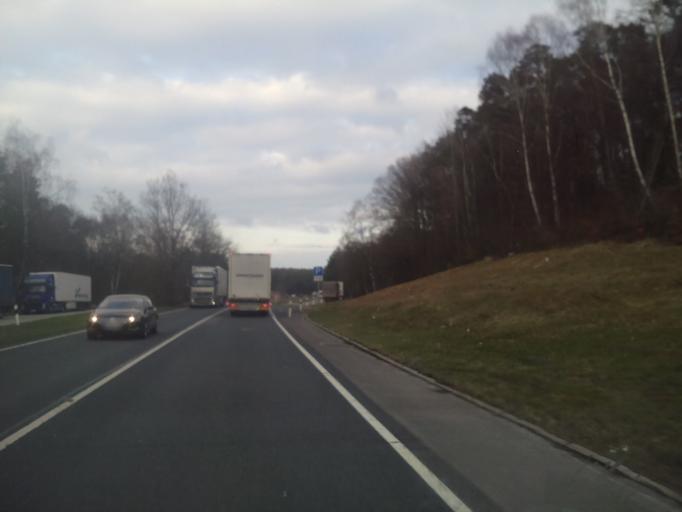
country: DE
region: Bavaria
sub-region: Upper Franconia
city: Frensdorf
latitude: 49.7674
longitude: 10.8781
